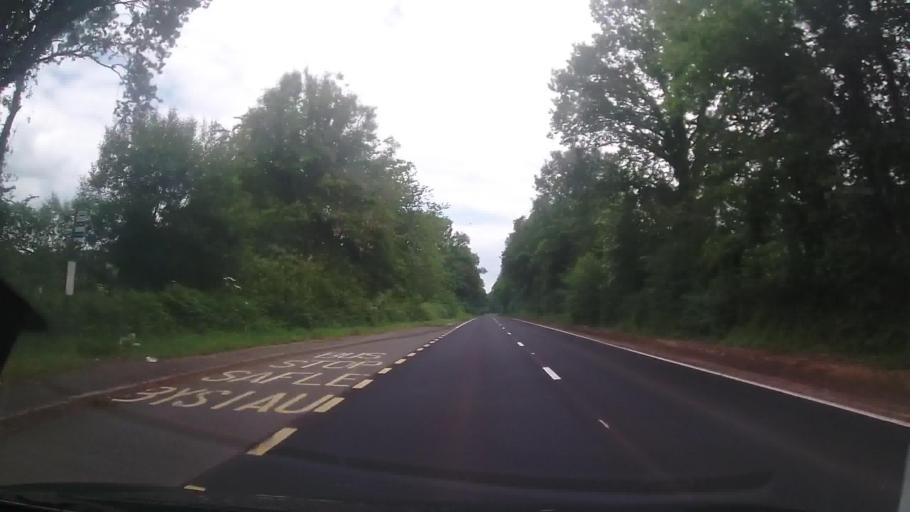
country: GB
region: England
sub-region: Herefordshire
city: Llancillo
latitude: 51.9046
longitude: -2.9551
